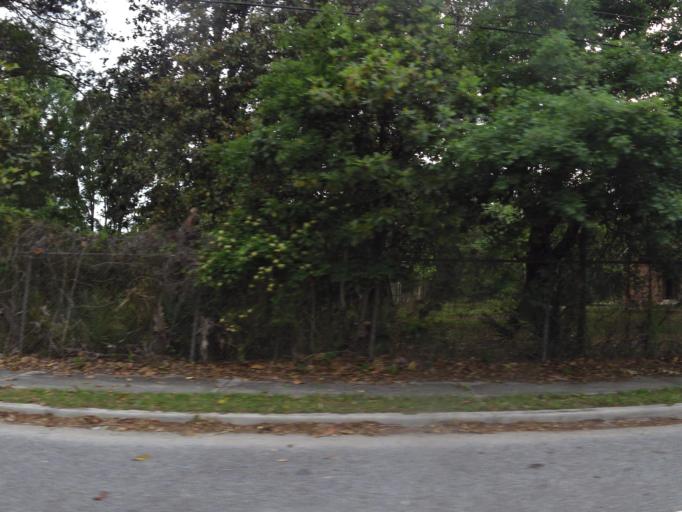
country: US
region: South Carolina
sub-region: Jasper County
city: Ridgeland
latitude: 32.4657
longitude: -81.1086
